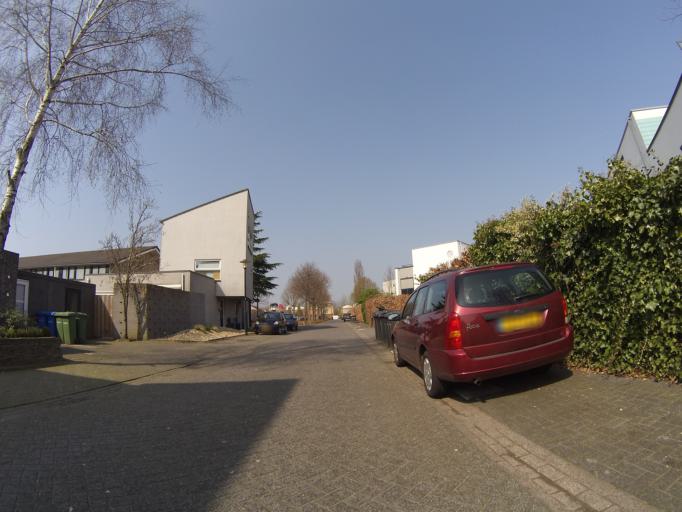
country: NL
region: Utrecht
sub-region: Gemeente Amersfoort
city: Hoogland
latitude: 52.1924
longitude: 5.3999
